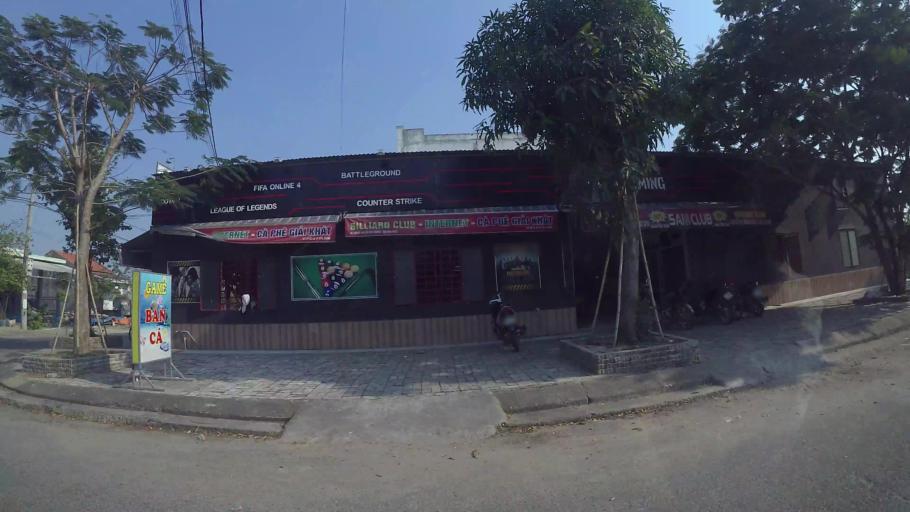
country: VN
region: Da Nang
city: Ngu Hanh Son
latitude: 15.9542
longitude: 108.2570
